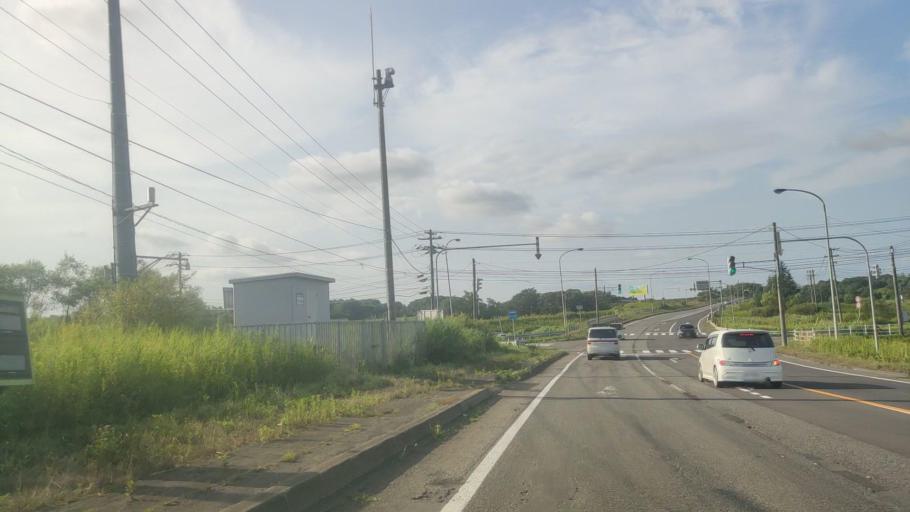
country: JP
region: Hokkaido
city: Chitose
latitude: 42.8849
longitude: 141.8122
